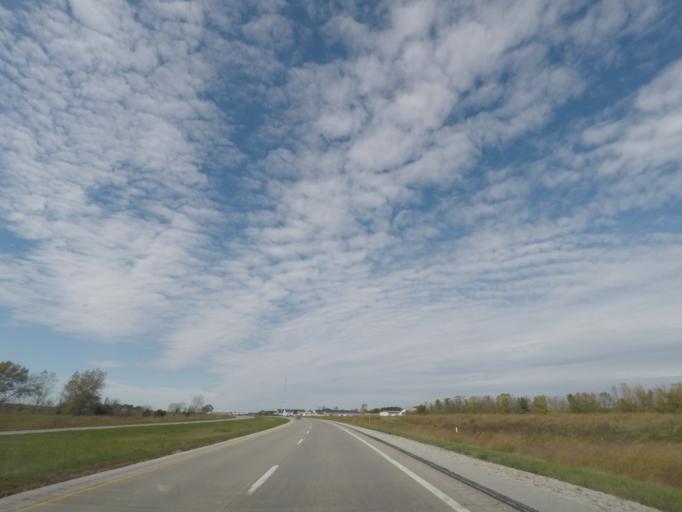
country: US
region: Iowa
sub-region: Story County
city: Ames
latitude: 42.0227
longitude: -93.7257
